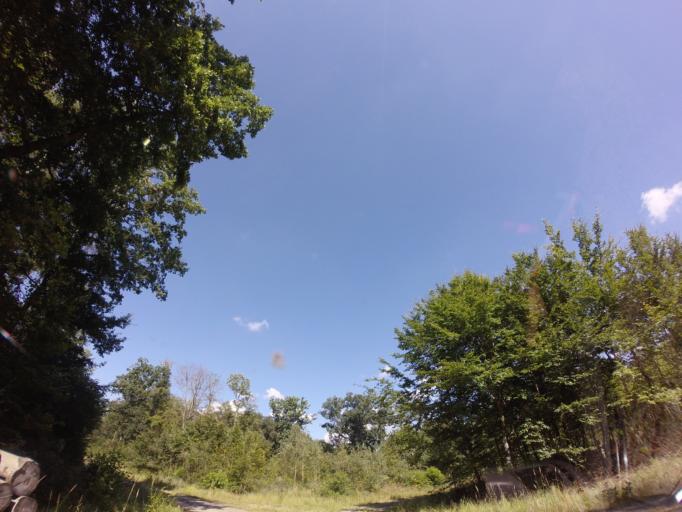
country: PL
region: West Pomeranian Voivodeship
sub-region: Powiat choszczenski
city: Recz
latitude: 53.2249
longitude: 15.6488
